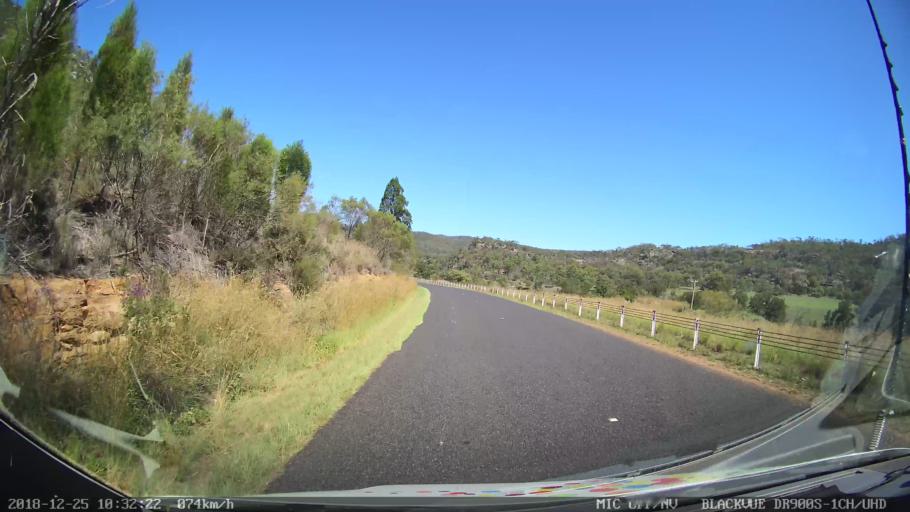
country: AU
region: New South Wales
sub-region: Upper Hunter Shire
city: Merriwa
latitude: -32.3770
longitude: 150.4195
